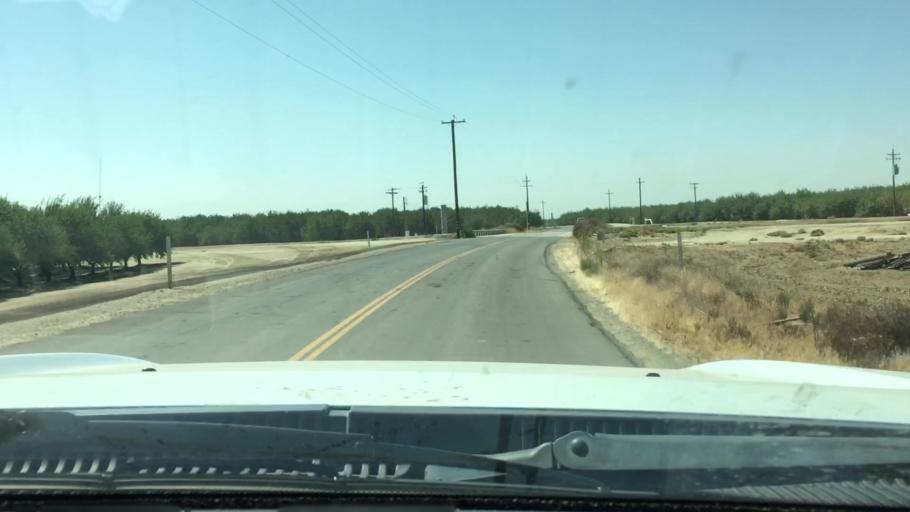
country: US
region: California
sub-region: Kern County
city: Shafter
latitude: 35.5507
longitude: -119.2767
